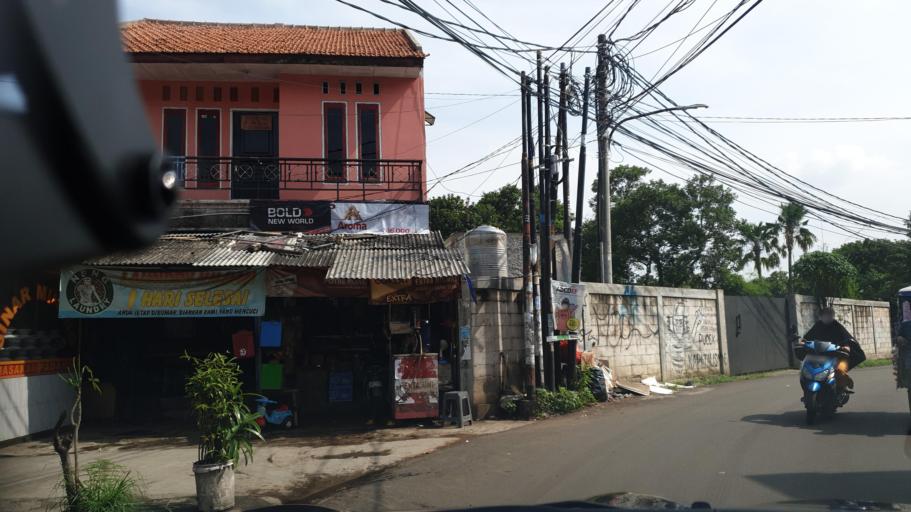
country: ID
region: West Java
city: Pamulang
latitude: -6.3032
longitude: 106.7654
